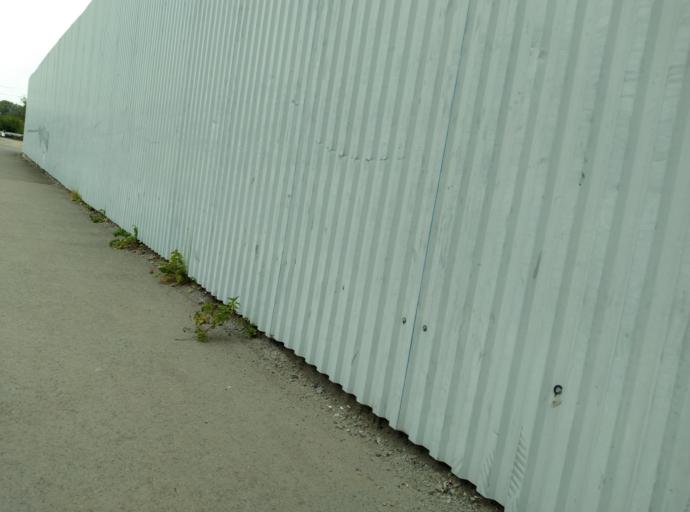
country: RU
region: Tomsk
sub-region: Tomskiy Rayon
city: Tomsk
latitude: 56.5254
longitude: 84.9575
